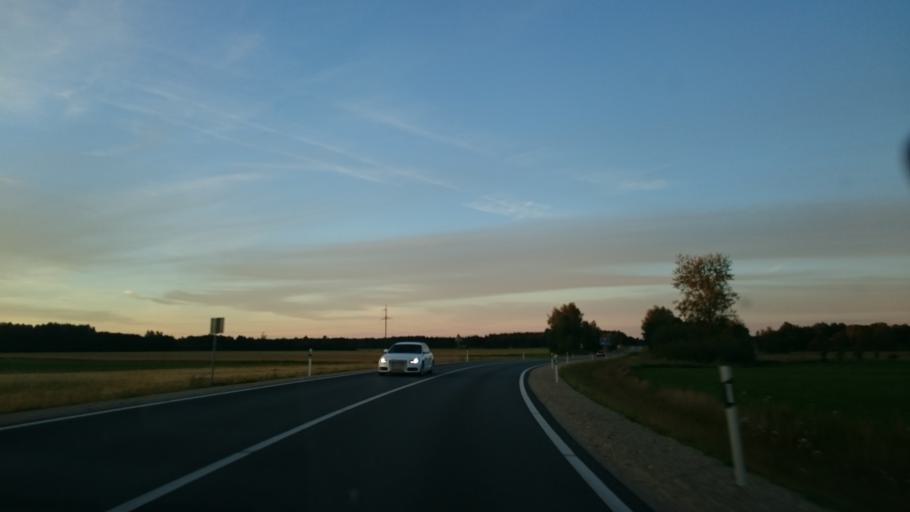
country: LV
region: Jaunpils
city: Jaunpils
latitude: 56.6777
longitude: 23.0897
